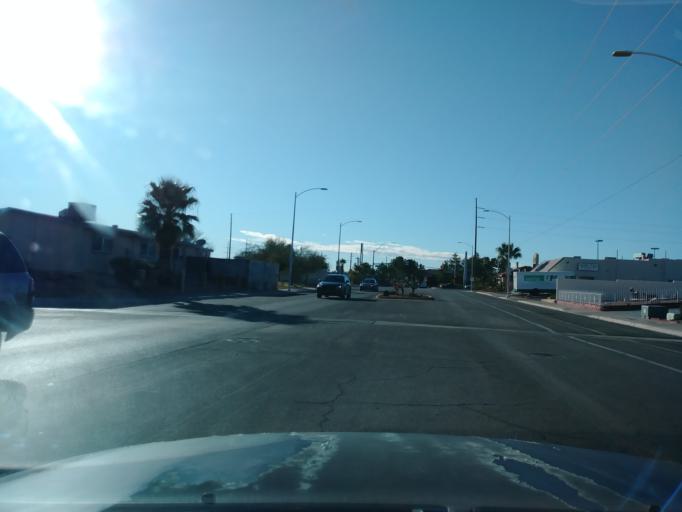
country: US
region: Nevada
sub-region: Clark County
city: Spring Valley
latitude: 36.1606
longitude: -115.2509
